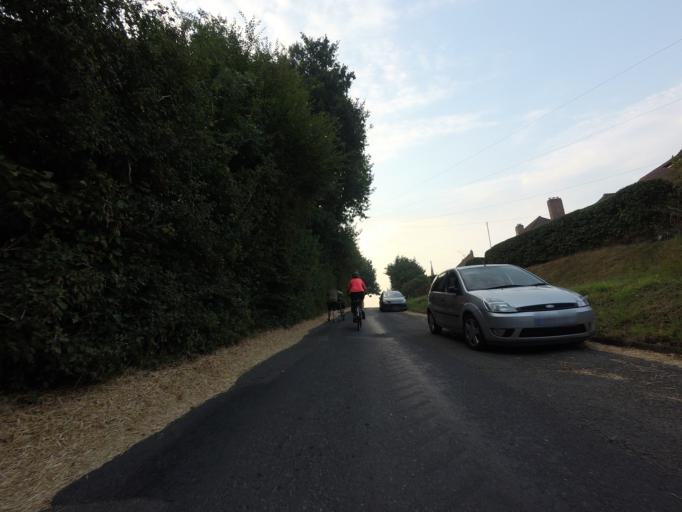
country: GB
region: England
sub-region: Kent
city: Lenham
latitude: 51.1867
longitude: 0.7136
